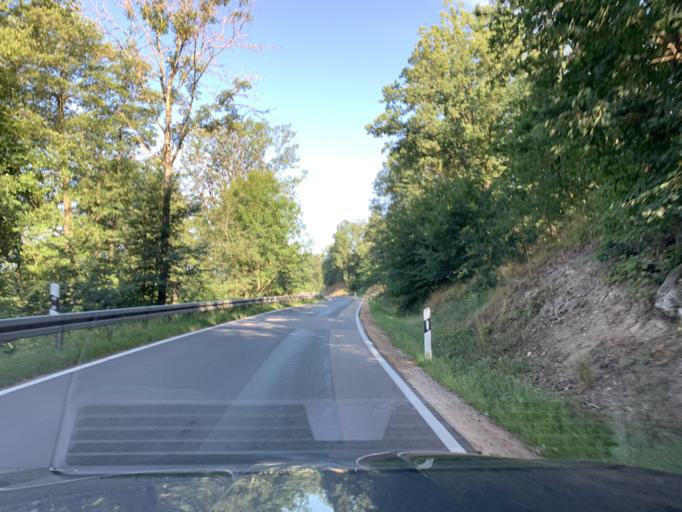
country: DE
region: Bavaria
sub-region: Upper Palatinate
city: Pettendorf
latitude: 49.3661
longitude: 12.3557
